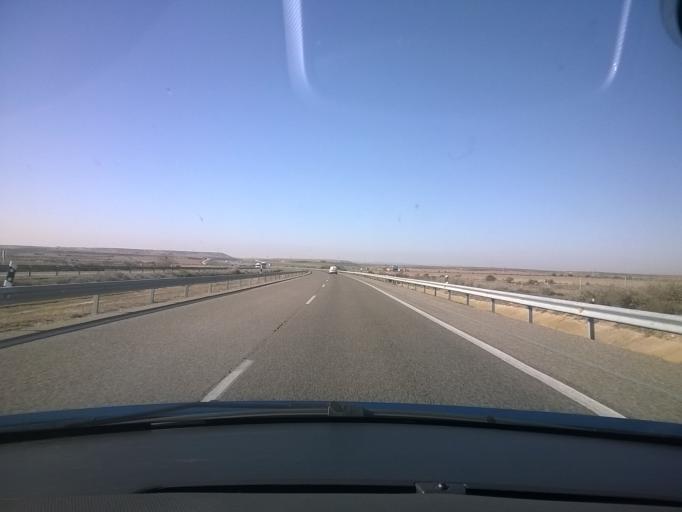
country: ES
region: Aragon
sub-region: Provincia de Zaragoza
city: Mequinensa / Mequinenza
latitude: 41.4749
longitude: 0.2099
